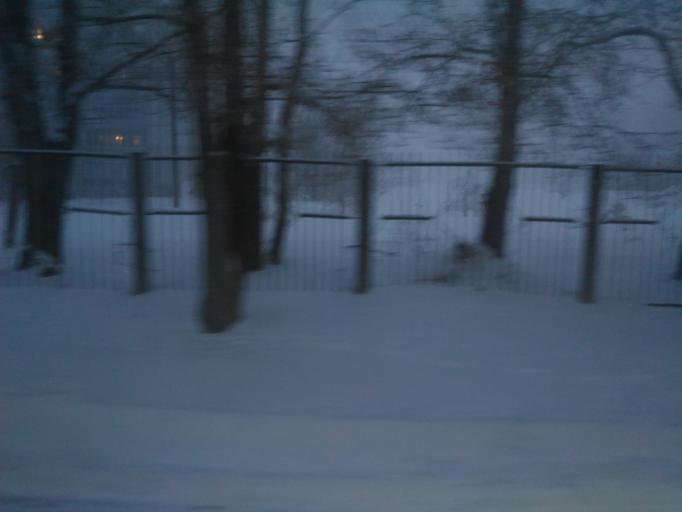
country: RU
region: Ulyanovsk
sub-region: Ulyanovskiy Rayon
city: Ulyanovsk
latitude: 54.3495
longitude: 48.3835
